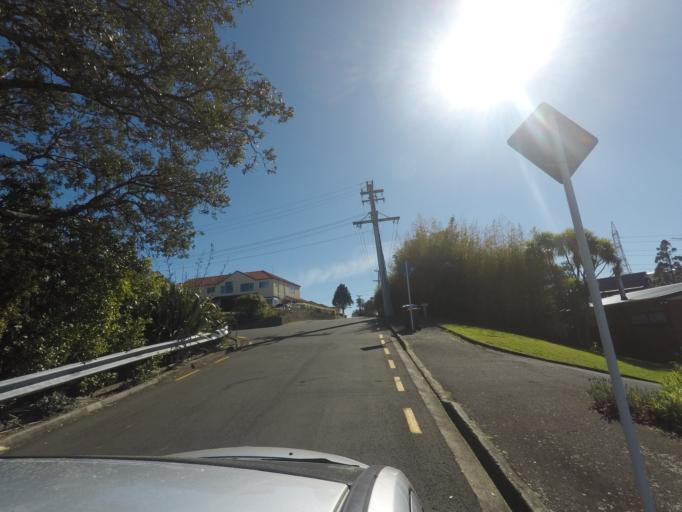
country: NZ
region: Auckland
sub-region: Auckland
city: Titirangi
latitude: -36.9317
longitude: 174.6976
